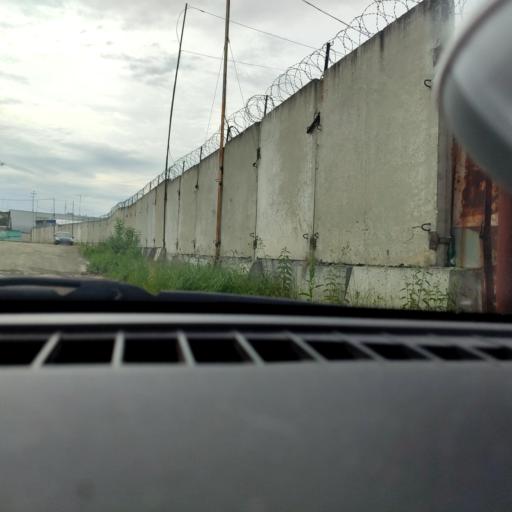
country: RU
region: Perm
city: Kondratovo
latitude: 57.9544
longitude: 56.1062
